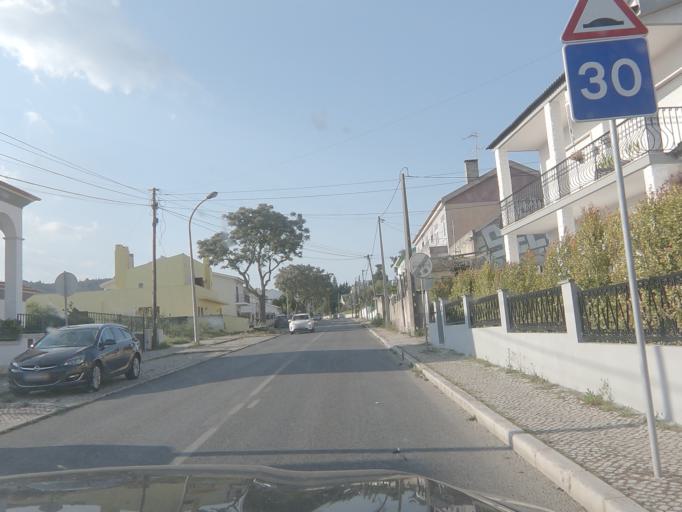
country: PT
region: Setubal
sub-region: Setubal
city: Setubal
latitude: 38.5406
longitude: -8.8976
